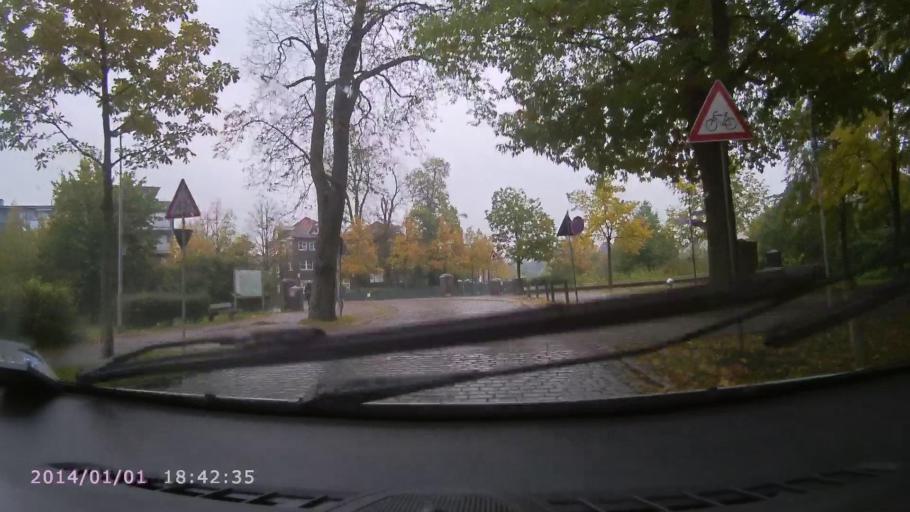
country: DE
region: Schleswig-Holstein
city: Ahrensburg
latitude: 53.6706
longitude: 10.2382
